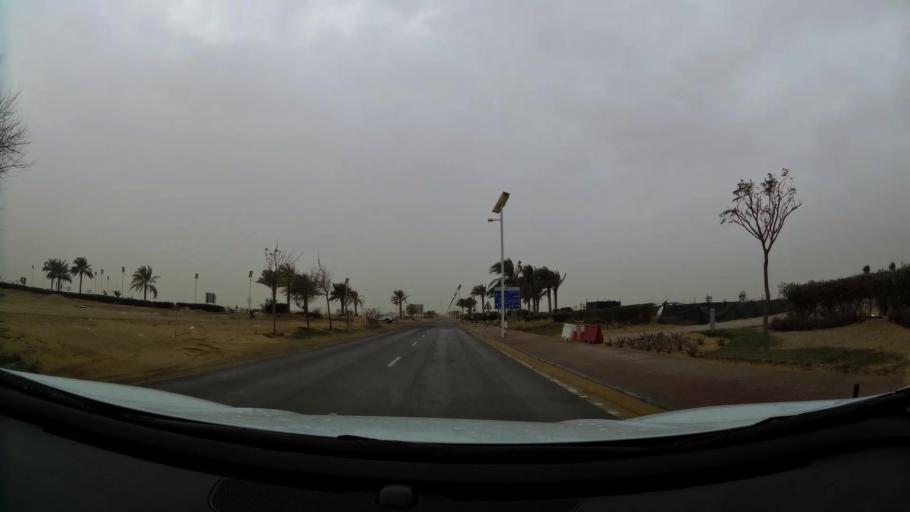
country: AE
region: Abu Dhabi
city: Abu Dhabi
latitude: 24.4347
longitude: 54.6132
